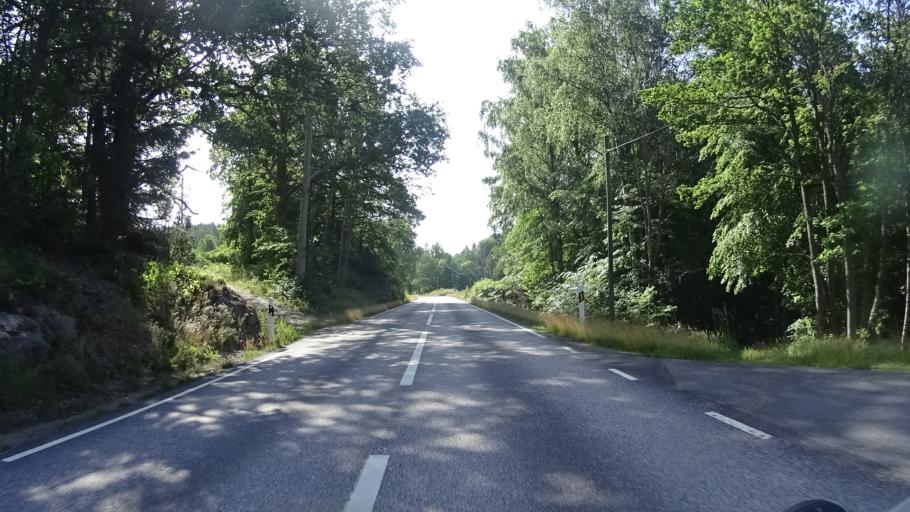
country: SE
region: Kalmar
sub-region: Vasterviks Kommun
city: Overum
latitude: 58.0183
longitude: 16.2512
